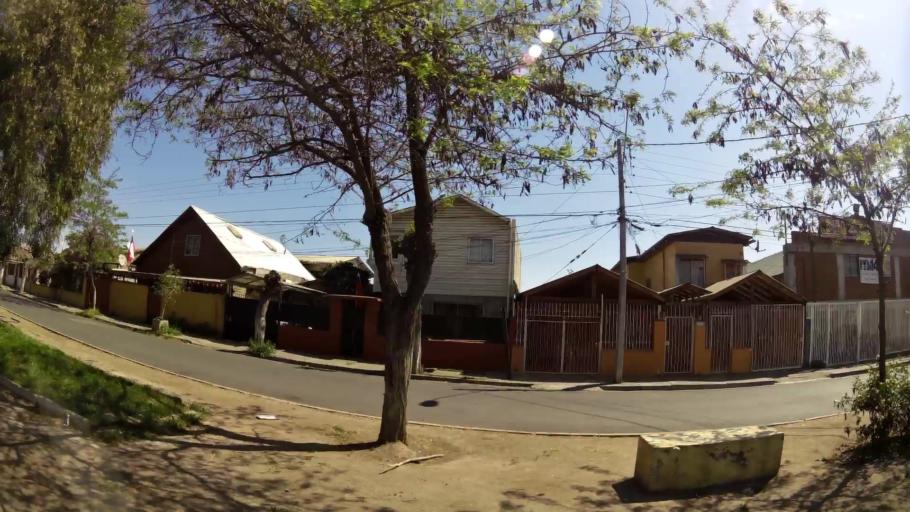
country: CL
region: Santiago Metropolitan
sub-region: Provincia de Santiago
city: La Pintana
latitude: -33.5332
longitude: -70.6372
